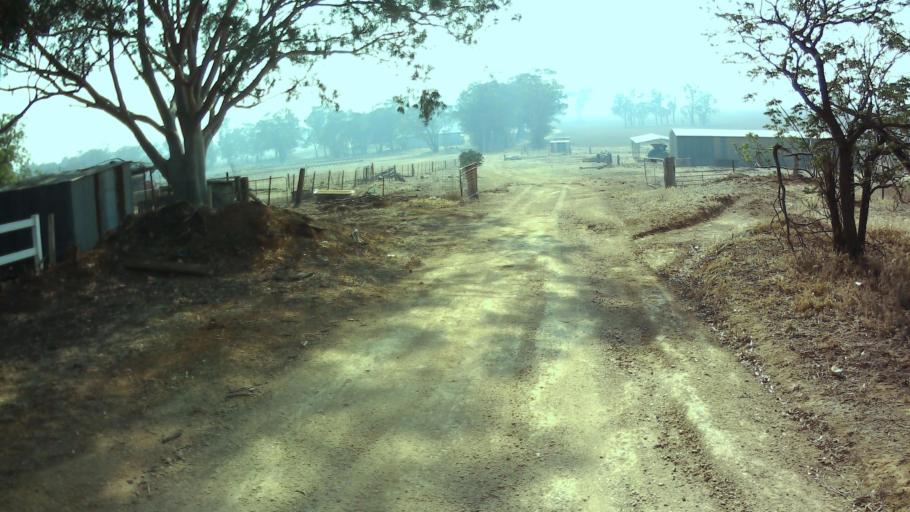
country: AU
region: New South Wales
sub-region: Weddin
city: Grenfell
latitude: -33.9121
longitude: 148.1883
